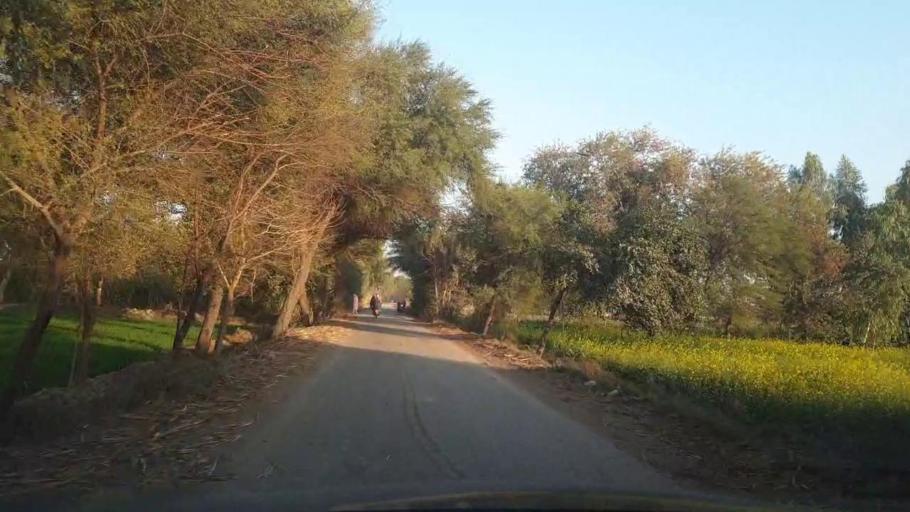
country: PK
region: Sindh
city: Ubauro
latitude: 28.1706
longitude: 69.5956
